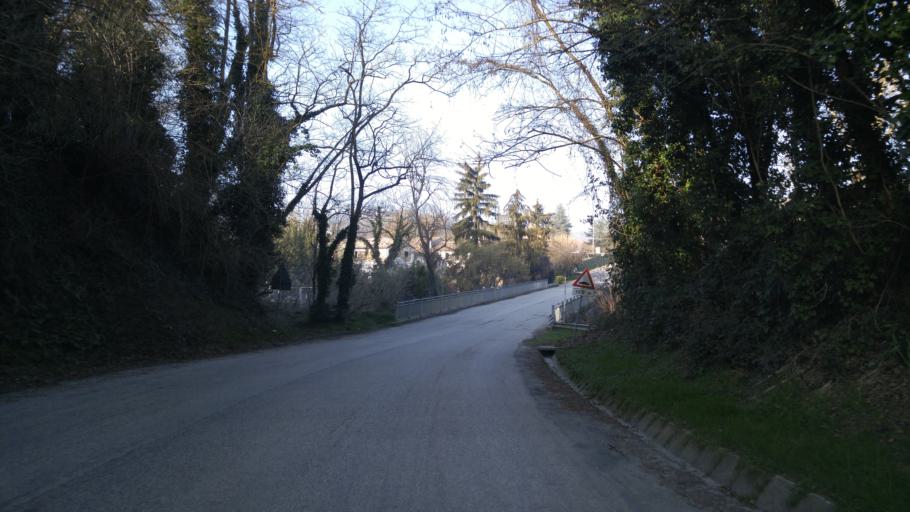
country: IT
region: The Marches
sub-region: Provincia di Pesaro e Urbino
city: Fenile
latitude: 43.8325
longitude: 12.9131
